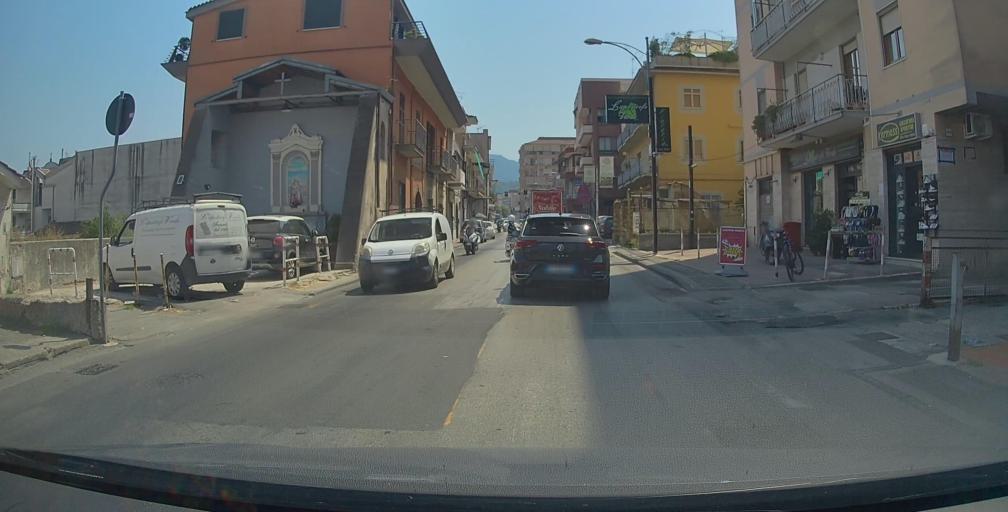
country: IT
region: Campania
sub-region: Provincia di Salerno
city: Nocera Superiore
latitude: 40.7405
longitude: 14.6618
